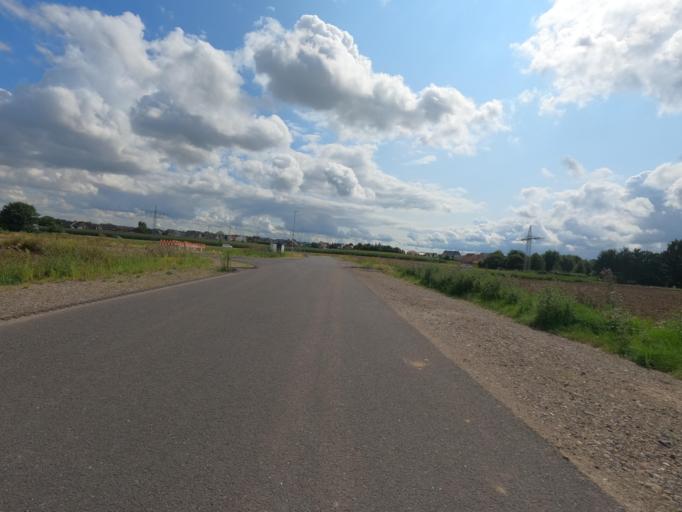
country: DE
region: North Rhine-Westphalia
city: Baesweiler
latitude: 50.9190
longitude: 6.1858
